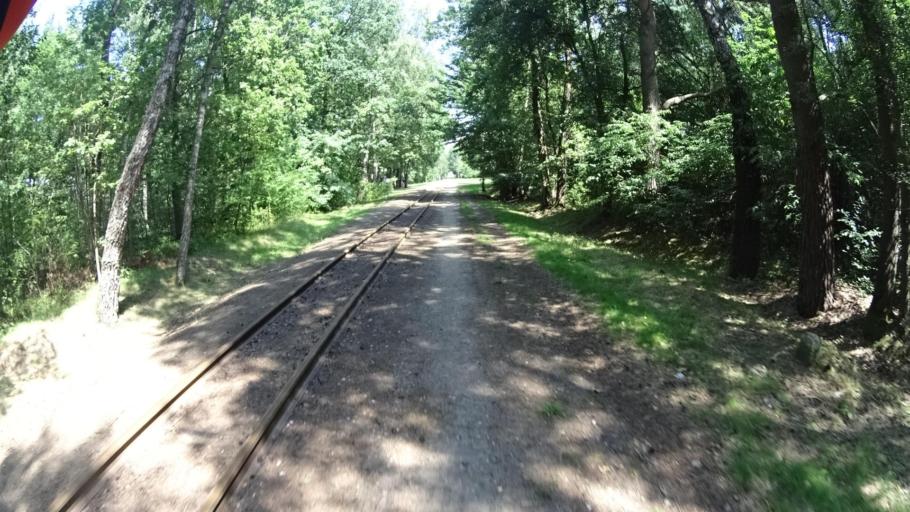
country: PL
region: Masovian Voivodeship
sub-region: Powiat piaseczynski
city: Lesznowola
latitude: 52.0185
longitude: 20.9334
